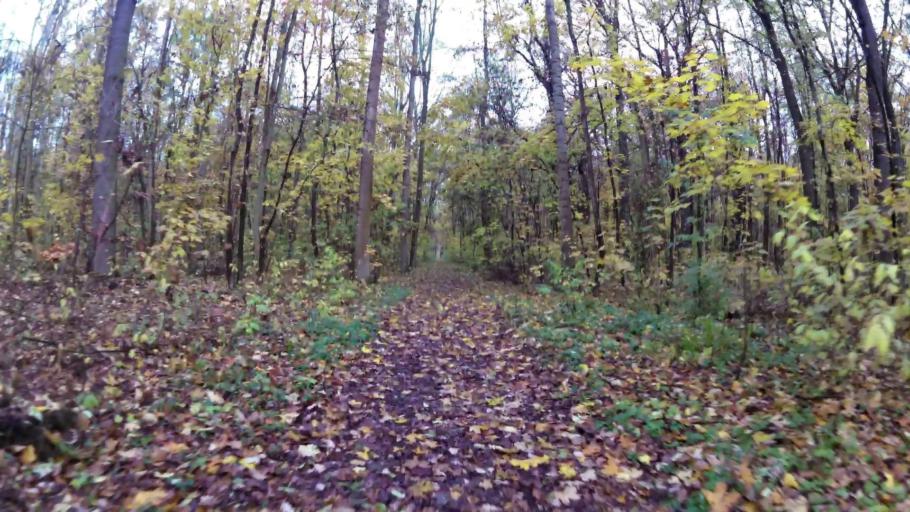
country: DE
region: Thuringia
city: Weimar
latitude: 50.9806
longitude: 11.3470
